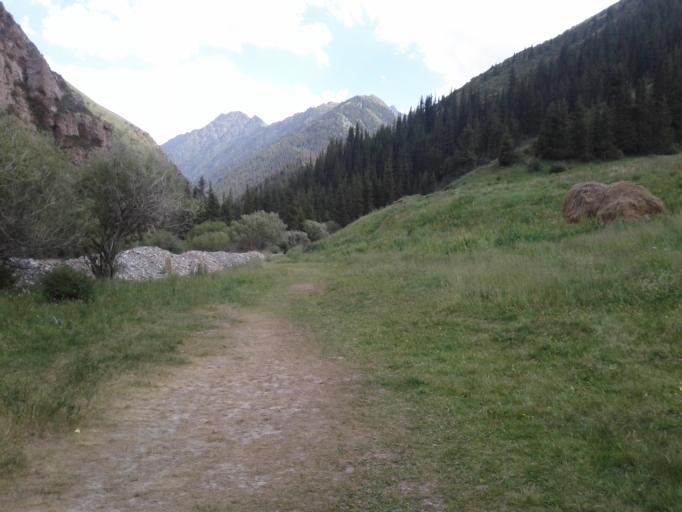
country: KG
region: Naryn
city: Naryn
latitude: 41.4575
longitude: 76.4527
